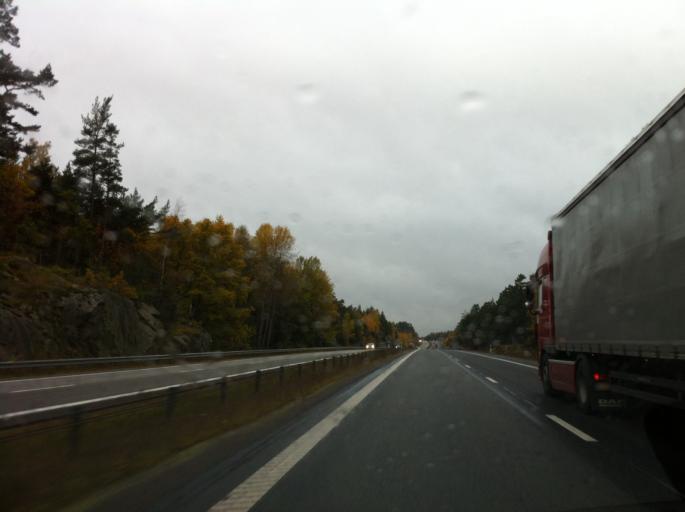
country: SE
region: Joenkoeping
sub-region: Jonkopings Kommun
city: Graenna
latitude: 57.9761
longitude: 14.3895
